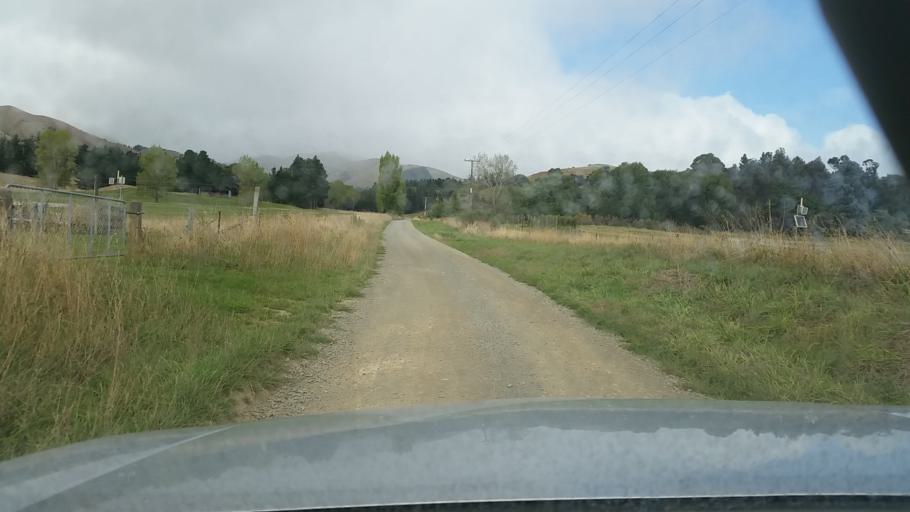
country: NZ
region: Marlborough
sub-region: Marlborough District
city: Blenheim
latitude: -41.7281
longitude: 173.9232
